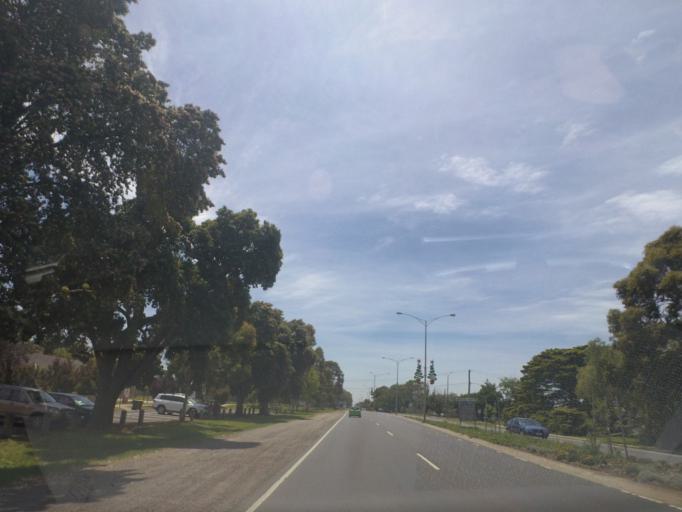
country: AU
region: Victoria
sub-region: Wyndham
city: Werribee
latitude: -37.8991
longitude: 144.6690
